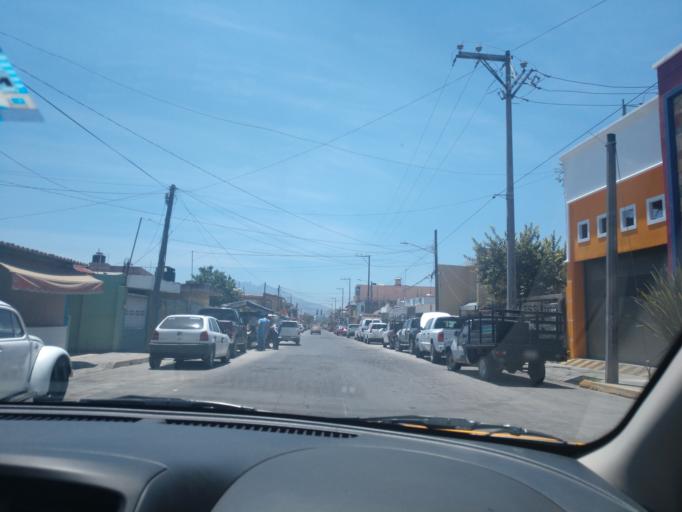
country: MX
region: Nayarit
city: Tepic
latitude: 21.5197
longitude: -104.9044
